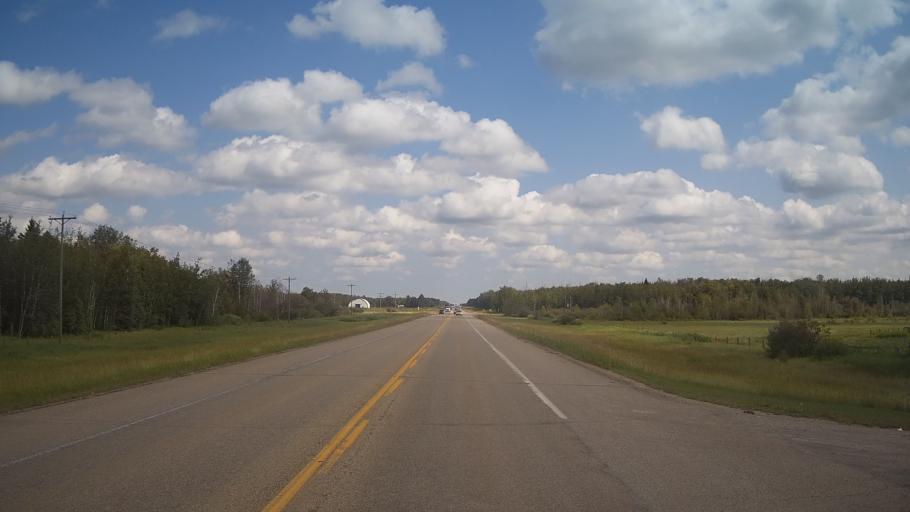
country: CA
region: Alberta
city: Sherwood Park
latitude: 53.3957
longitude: -113.0795
